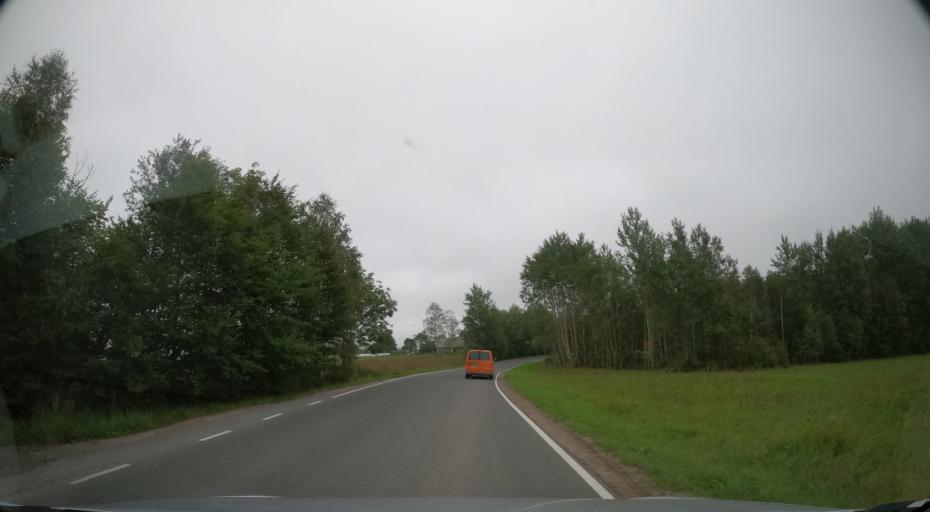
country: PL
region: Pomeranian Voivodeship
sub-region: Powiat wejherowski
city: Szemud
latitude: 54.5025
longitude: 18.1687
